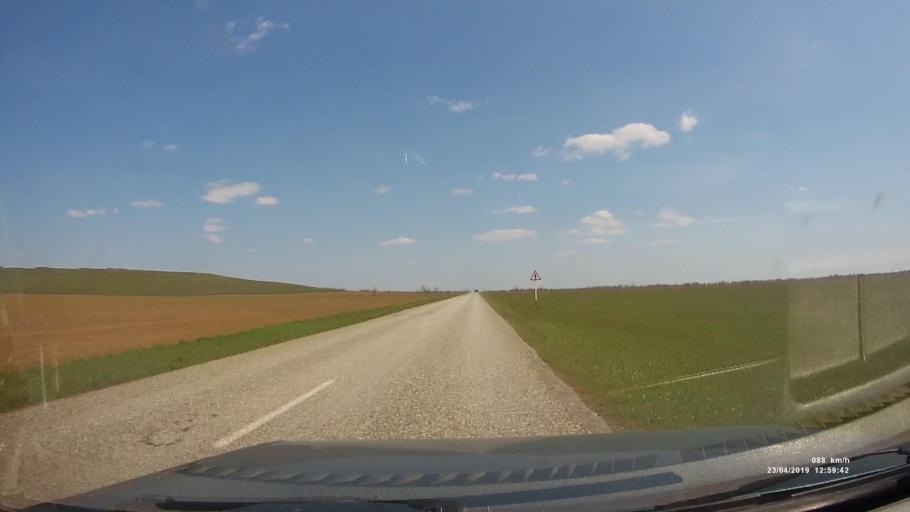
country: RU
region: Kalmykiya
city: Yashalta
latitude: 46.6042
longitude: 42.6202
